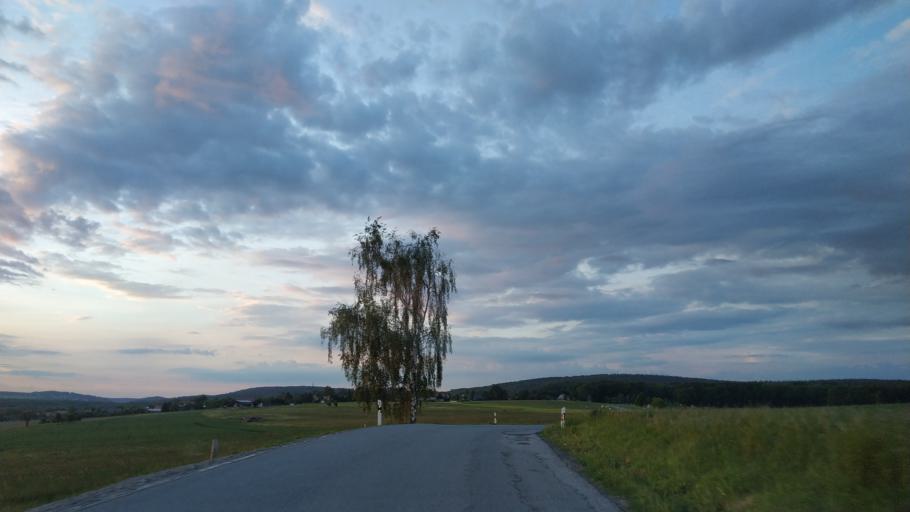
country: DE
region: Saxony
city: Lohmen
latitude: 50.9779
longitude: 14.0213
